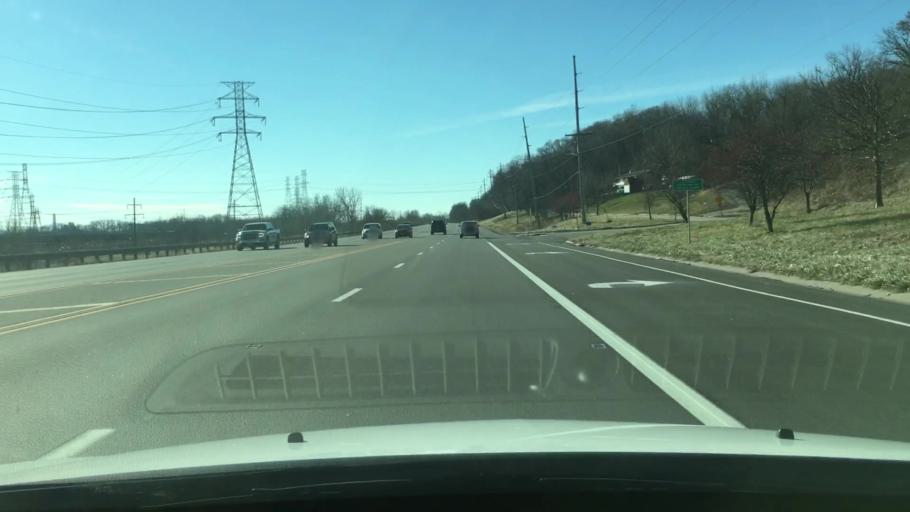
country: US
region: Illinois
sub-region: Tazewell County
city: Pekin
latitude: 40.6019
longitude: -89.6669
